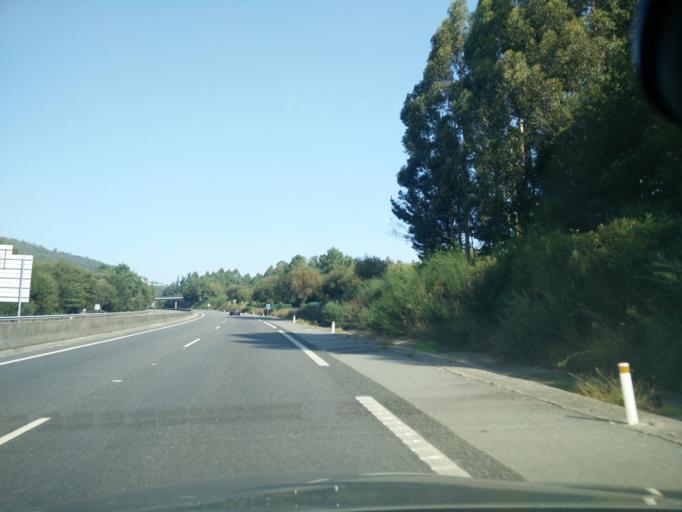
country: ES
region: Galicia
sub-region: Provincia da Coruna
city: Mino
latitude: 43.3842
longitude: -8.1779
